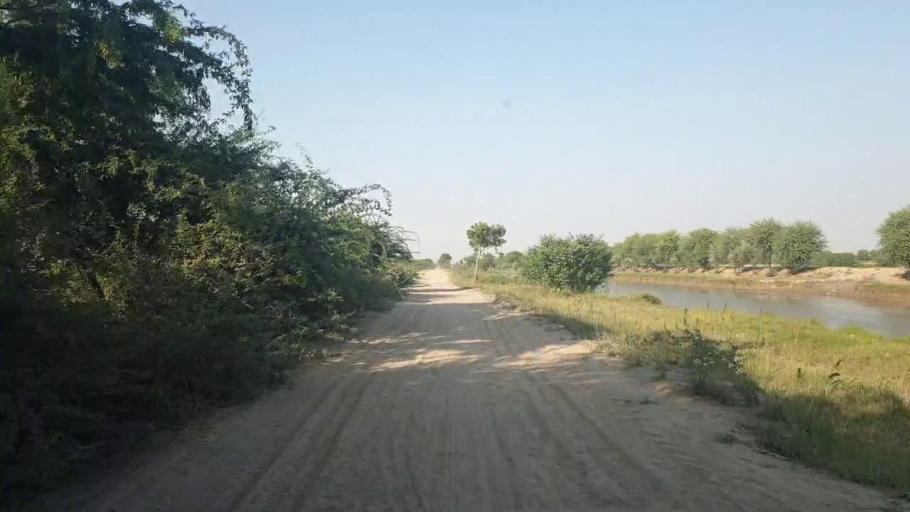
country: PK
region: Sindh
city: Badin
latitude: 24.6295
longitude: 68.8149
